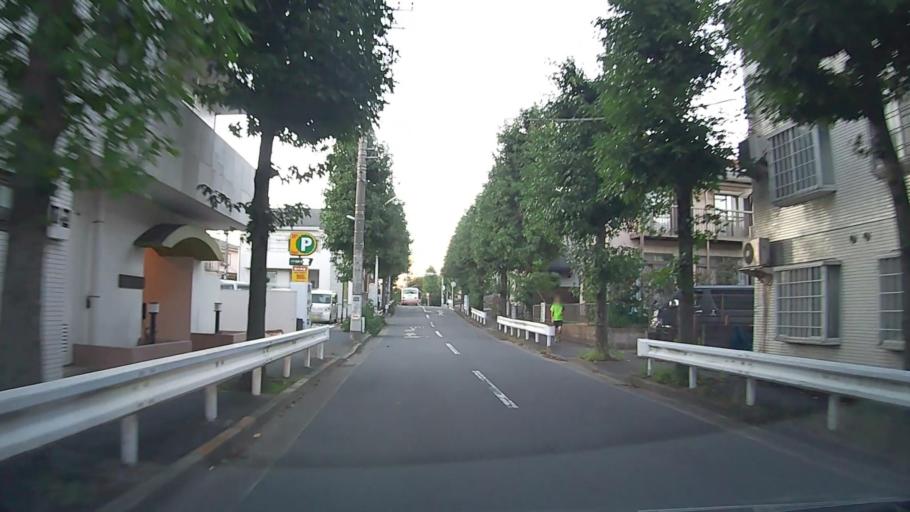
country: JP
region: Tokyo
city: Chofugaoka
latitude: 35.6307
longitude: 139.5300
